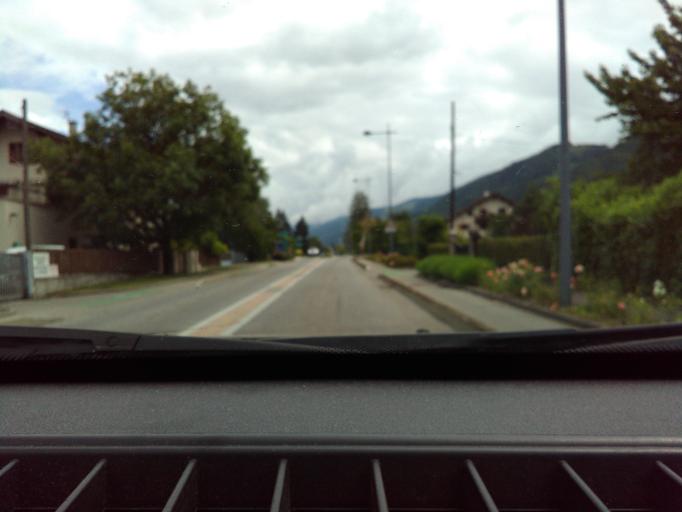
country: FR
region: Rhone-Alpes
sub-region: Departement de l'Isere
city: Gieres
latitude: 45.1886
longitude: 5.8092
